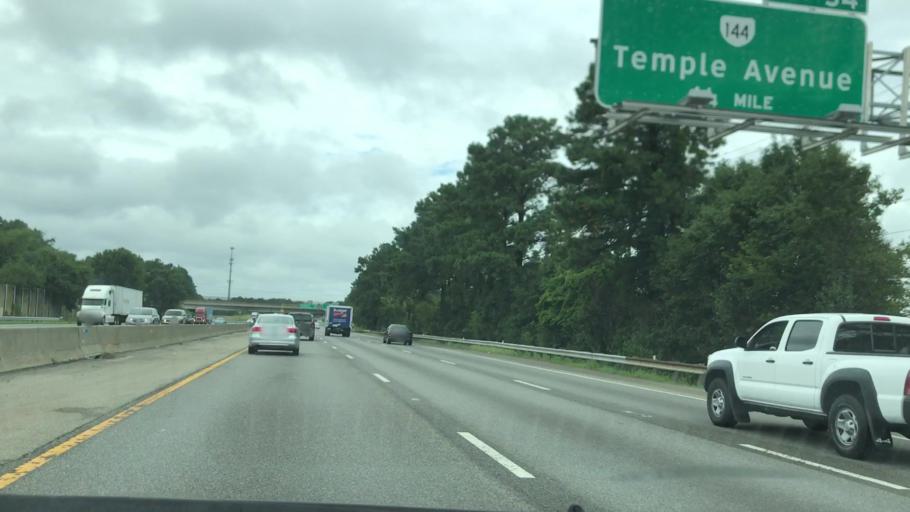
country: US
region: Virginia
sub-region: City of Colonial Heights
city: Colonial Heights
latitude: 37.2515
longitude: -77.3948
